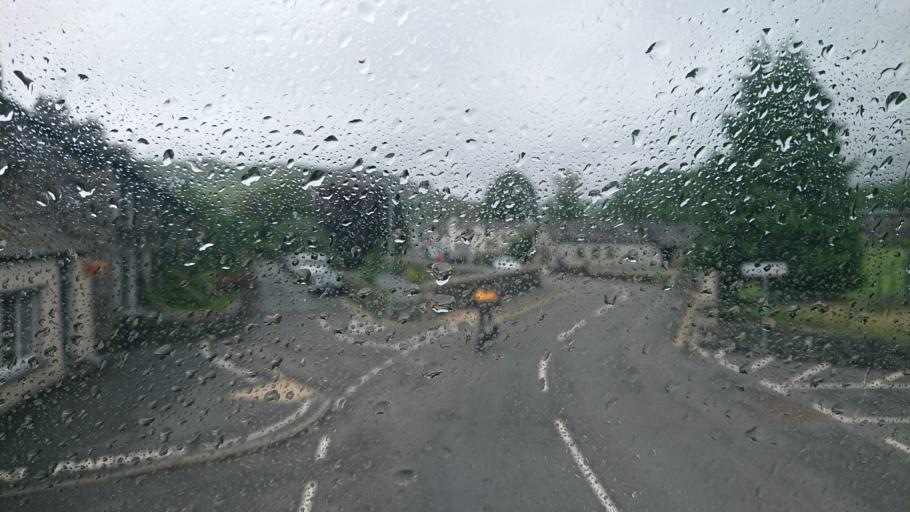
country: GB
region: England
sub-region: Cumbria
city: Kendal
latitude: 54.3750
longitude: -2.8141
